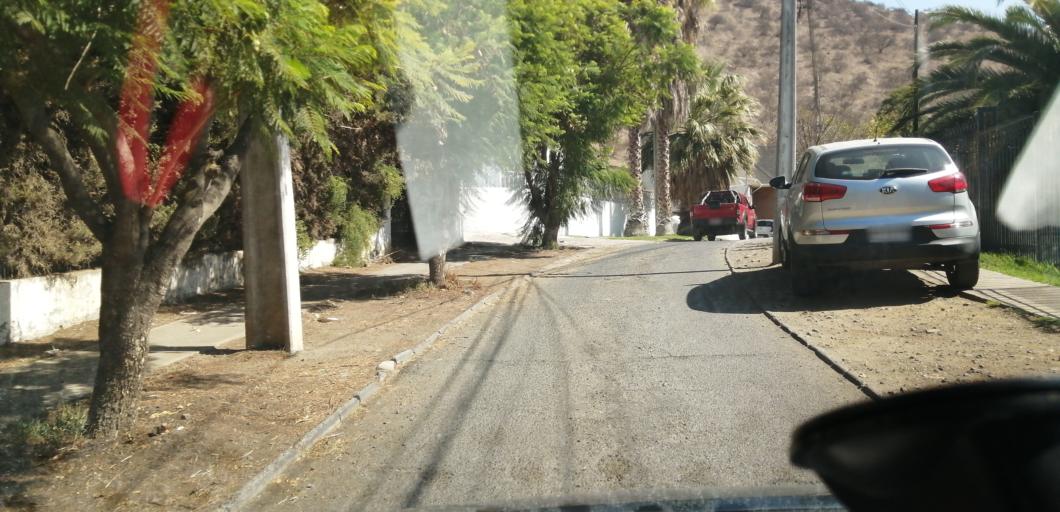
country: CL
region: Santiago Metropolitan
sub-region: Provincia de Santiago
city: Lo Prado
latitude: -33.4545
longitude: -70.8241
